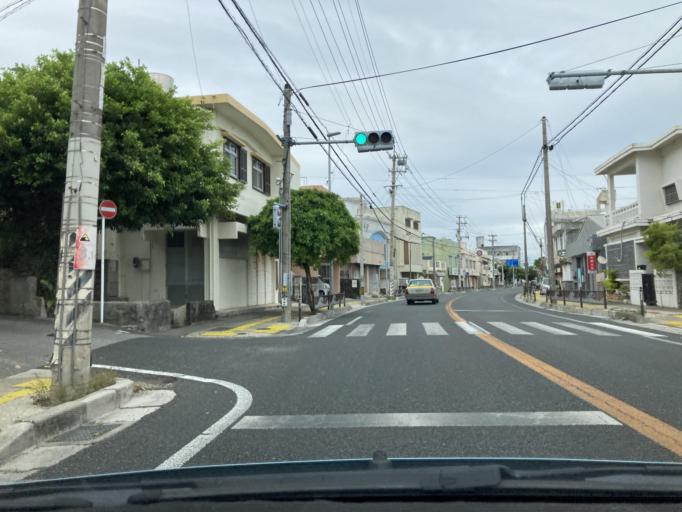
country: JP
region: Okinawa
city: Itoman
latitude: 26.1332
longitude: 127.6701
